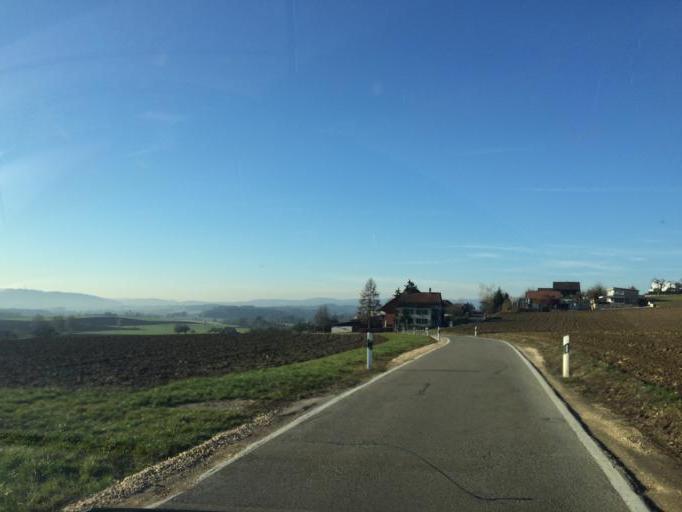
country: CH
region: Thurgau
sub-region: Frauenfeld District
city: Diessenhofen
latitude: 47.7021
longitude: 8.7304
